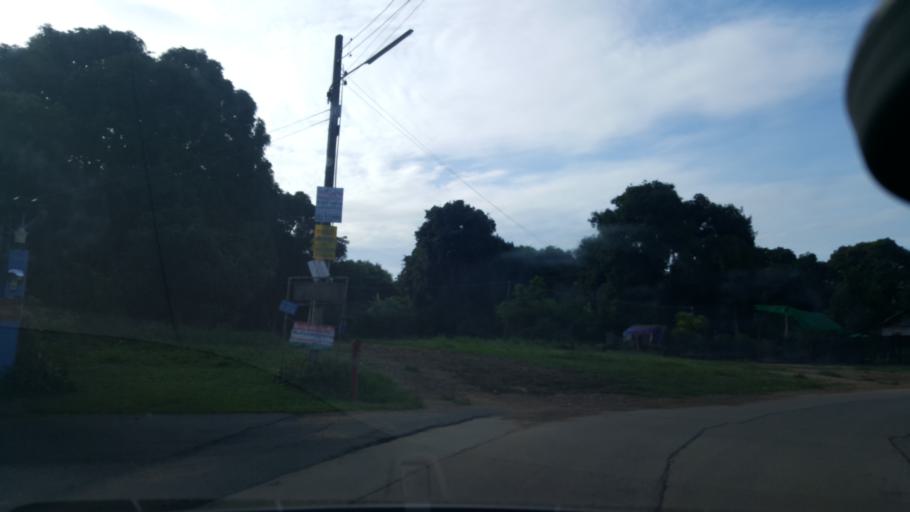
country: TH
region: Chon Buri
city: Sattahip
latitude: 12.6847
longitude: 100.9118
